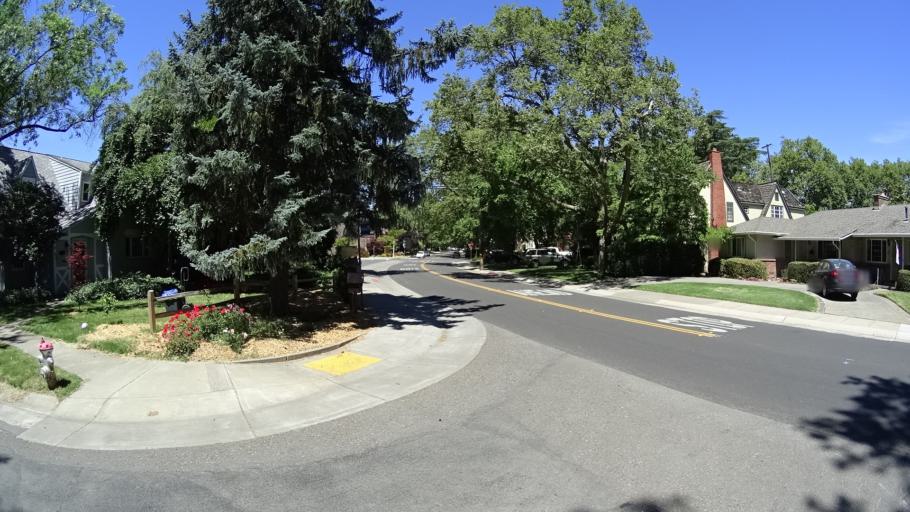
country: US
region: California
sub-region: Sacramento County
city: Sacramento
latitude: 38.5760
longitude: -121.4543
